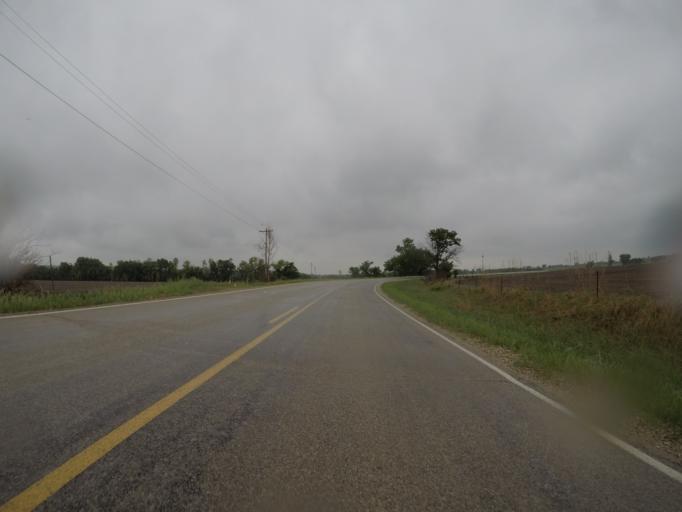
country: US
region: Kansas
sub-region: Pottawatomie County
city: Wamego
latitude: 39.3782
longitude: -96.2072
